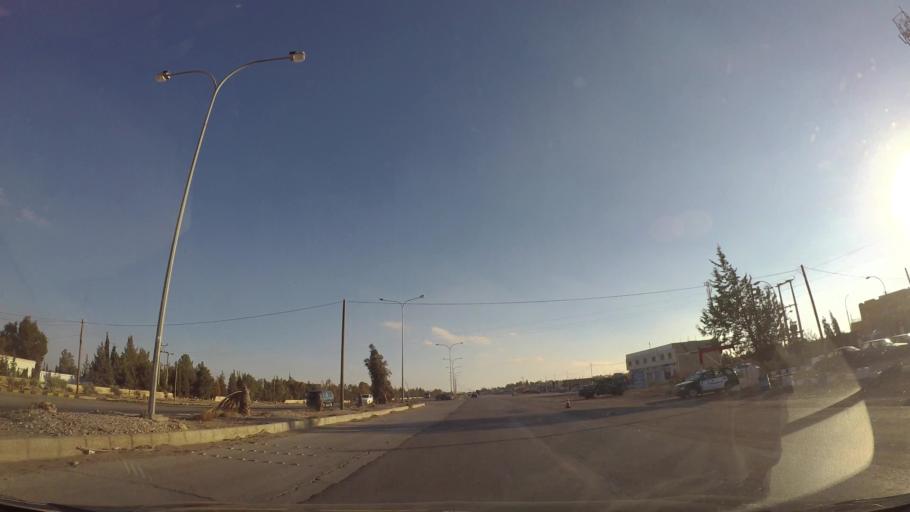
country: JO
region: Tafielah
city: Busayra
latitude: 30.6042
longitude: 35.8057
